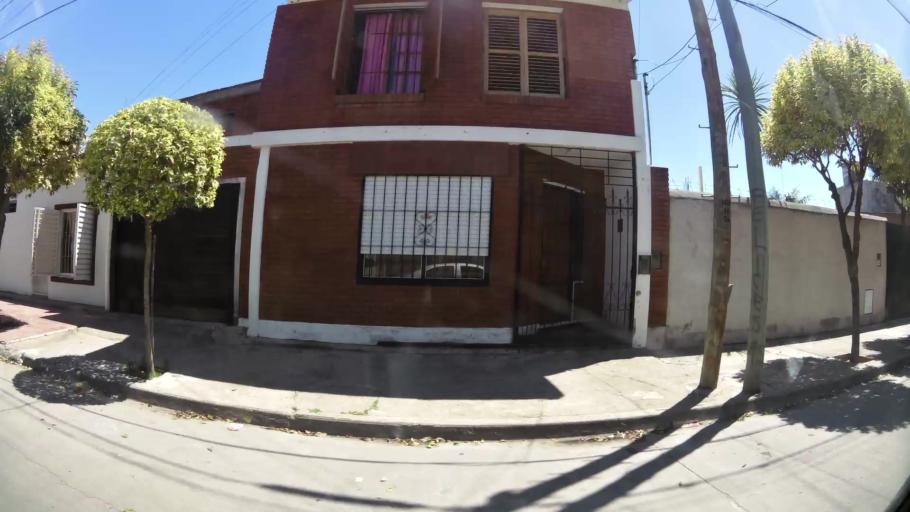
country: AR
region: Cordoba
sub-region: Departamento de Capital
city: Cordoba
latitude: -31.4286
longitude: -64.1229
